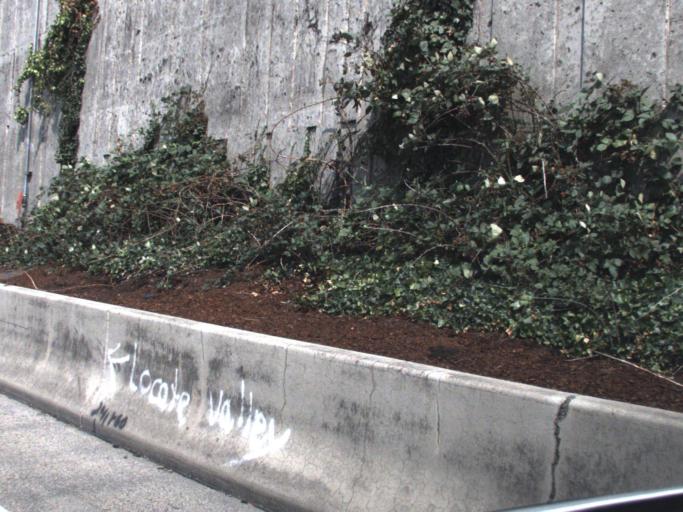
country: US
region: Washington
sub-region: King County
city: Mercer Island
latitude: 47.5906
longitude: -122.2387
